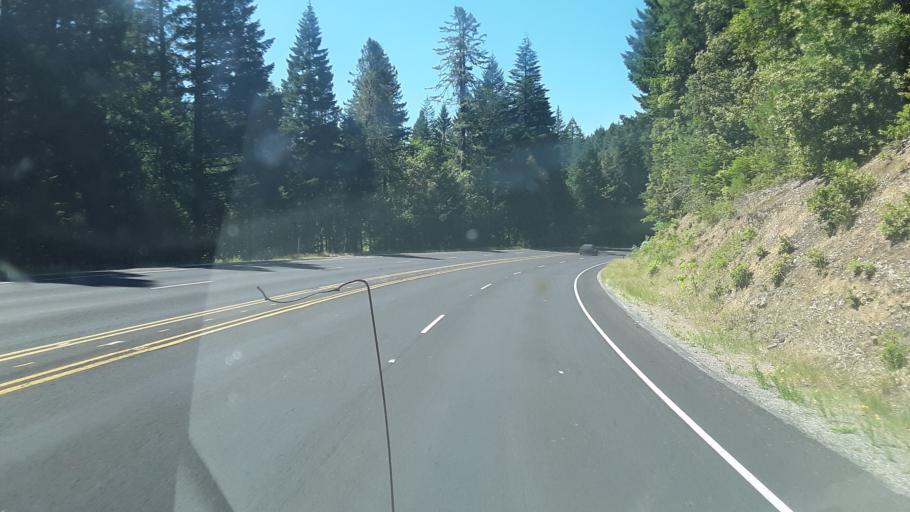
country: US
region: Oregon
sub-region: Josephine County
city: Cave Junction
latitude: 41.9153
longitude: -123.7686
